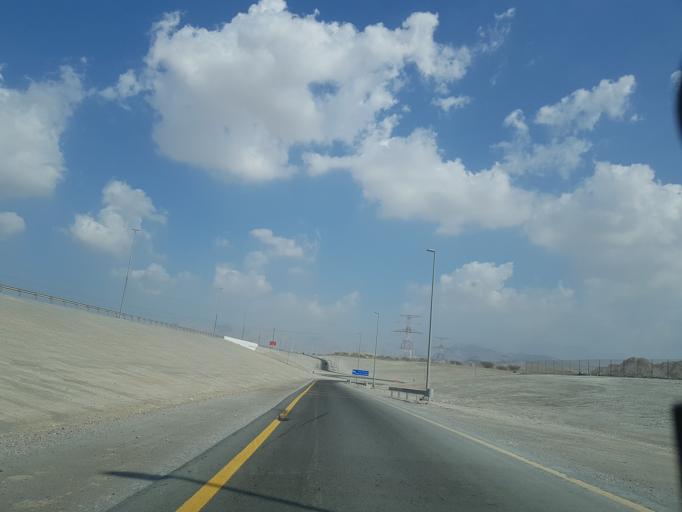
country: AE
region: Ra's al Khaymah
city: Ras al-Khaimah
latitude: 25.7611
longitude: 56.0220
